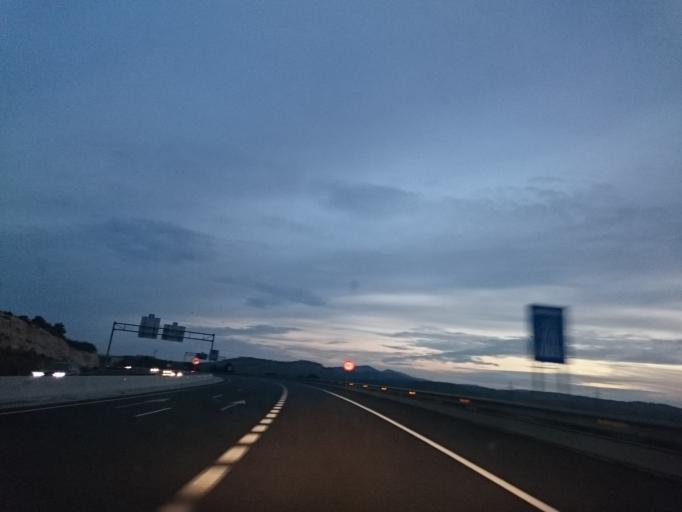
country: ES
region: Catalonia
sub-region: Provincia de Barcelona
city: Vilafranca del Penedes
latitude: 41.3282
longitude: 1.7117
